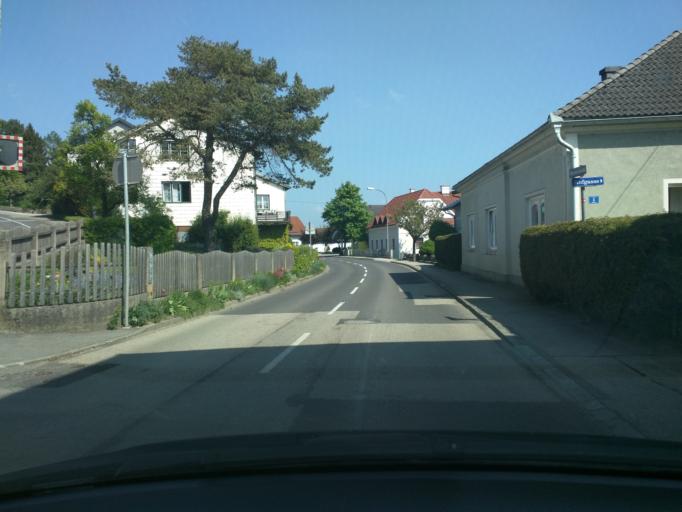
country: AT
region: Lower Austria
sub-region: Politischer Bezirk Amstetten
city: Sankt Georgen am Ybbsfelde
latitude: 48.1290
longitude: 14.9528
